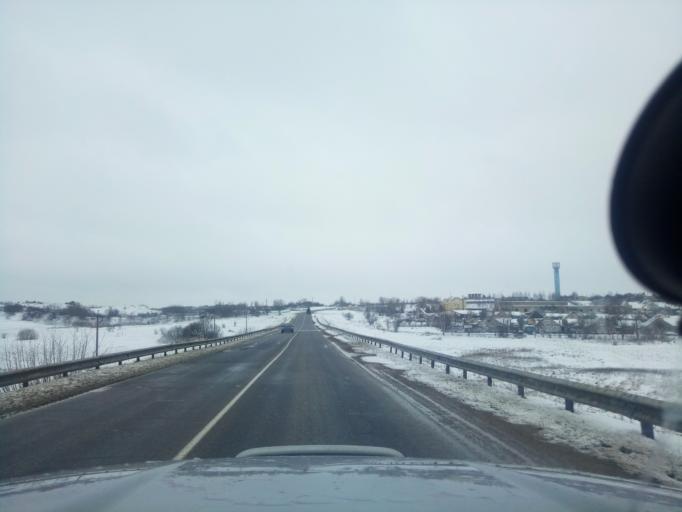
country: BY
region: Minsk
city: Kapyl'
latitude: 53.1437
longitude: 27.0796
